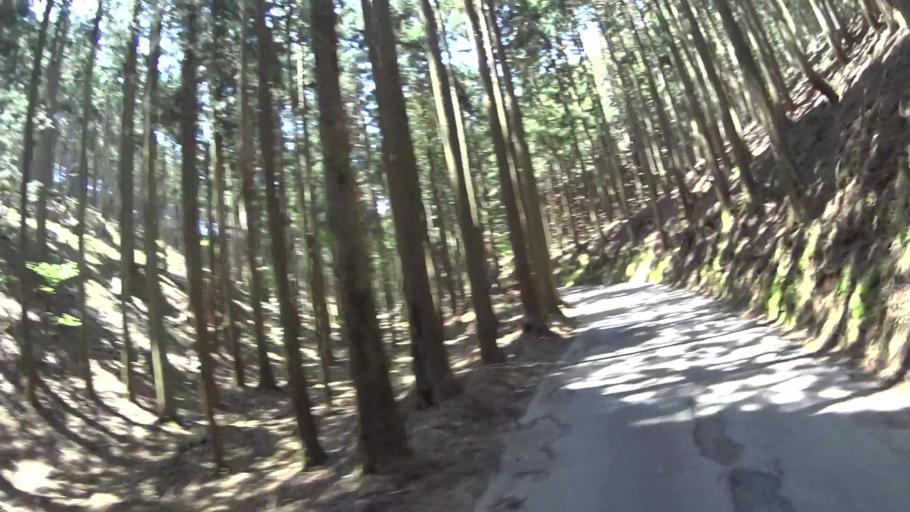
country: JP
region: Shiga Prefecture
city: Kitahama
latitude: 35.1555
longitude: 135.7993
